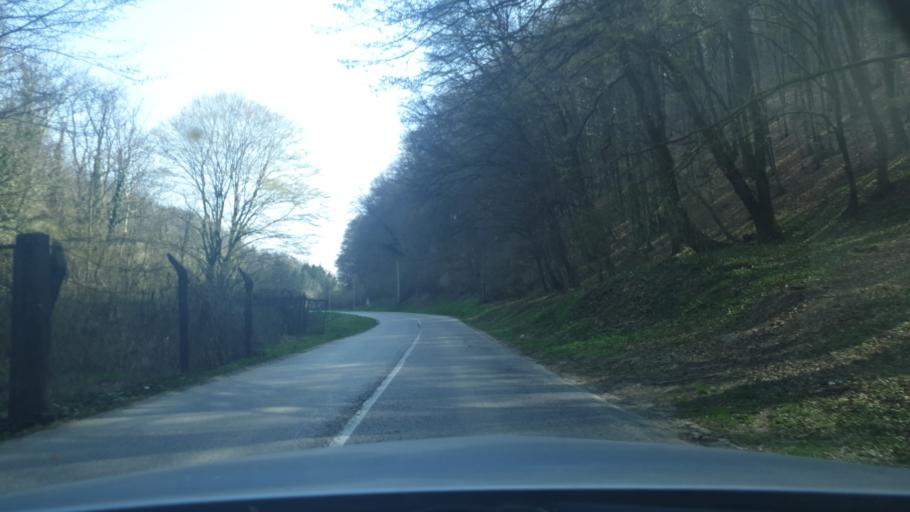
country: RS
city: Vrdnik
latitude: 45.1379
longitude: 19.7757
